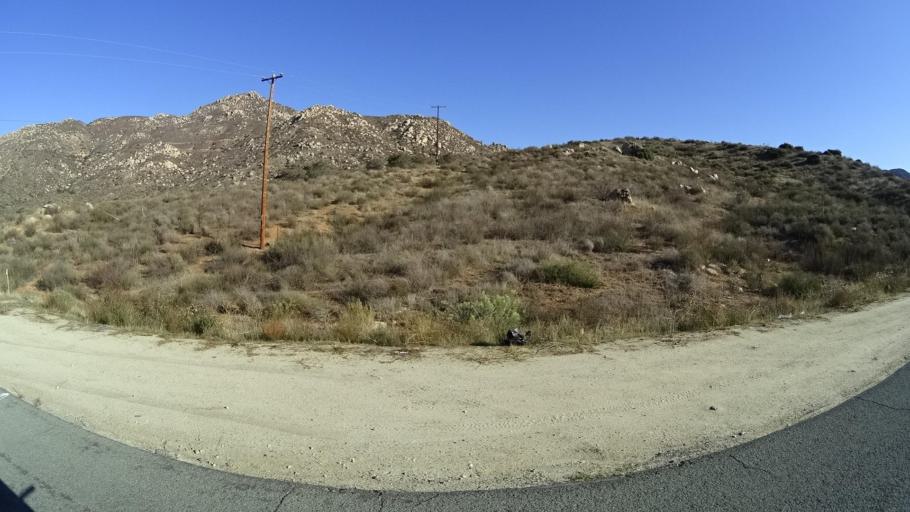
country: MX
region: Baja California
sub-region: Tecate
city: Lomas de Santa Anita
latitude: 32.6108
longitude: -116.7024
